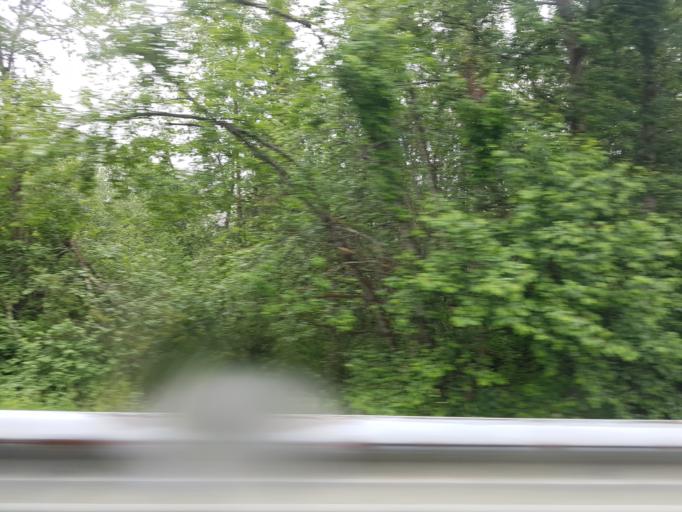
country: NO
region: Nord-Trondelag
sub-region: Stjordal
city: Stjordalshalsen
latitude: 63.3925
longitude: 10.9920
